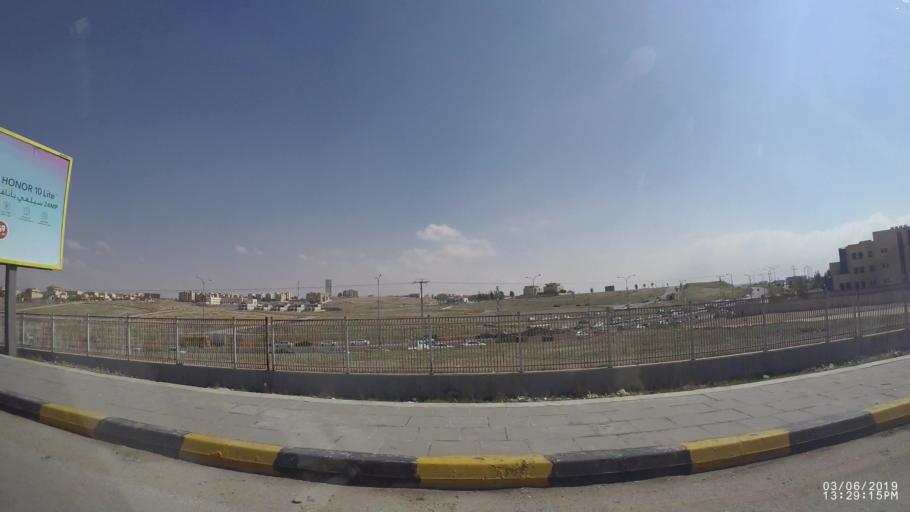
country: JO
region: Zarqa
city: Zarqa
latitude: 32.0779
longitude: 36.1039
